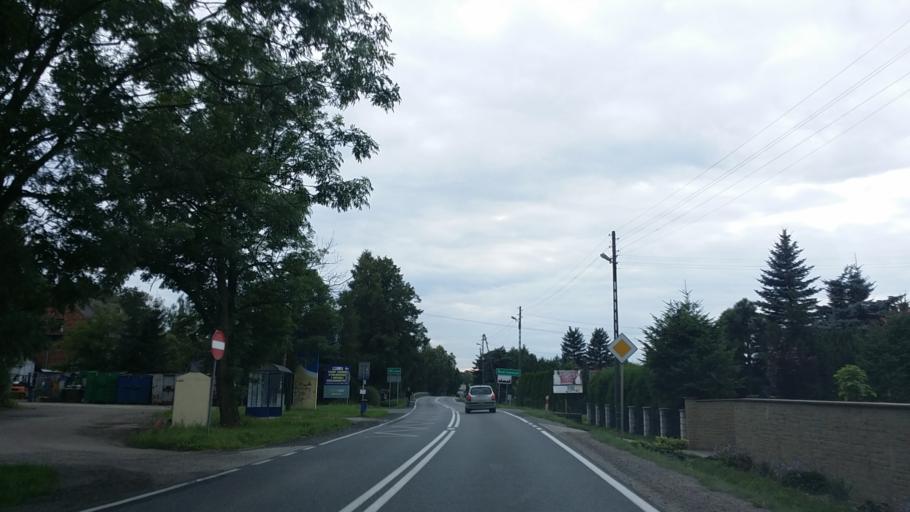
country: PL
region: Lesser Poland Voivodeship
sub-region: Powiat krakowski
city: Rzozow
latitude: 49.9688
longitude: 19.7855
